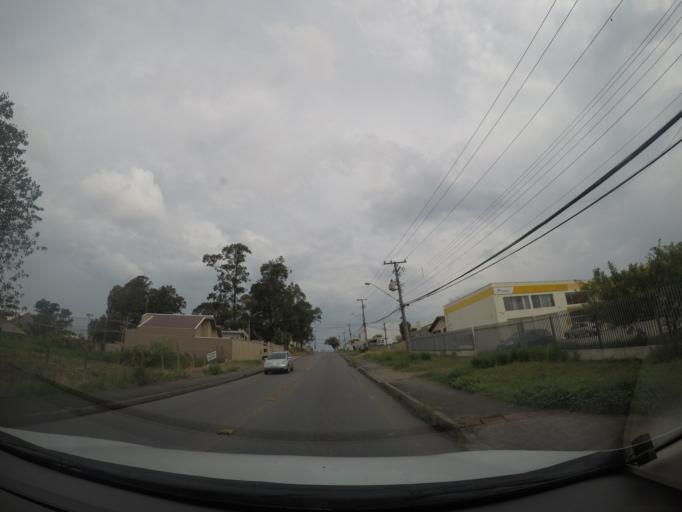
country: BR
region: Parana
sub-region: Sao Jose Dos Pinhais
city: Sao Jose dos Pinhais
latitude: -25.5235
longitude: -49.2611
